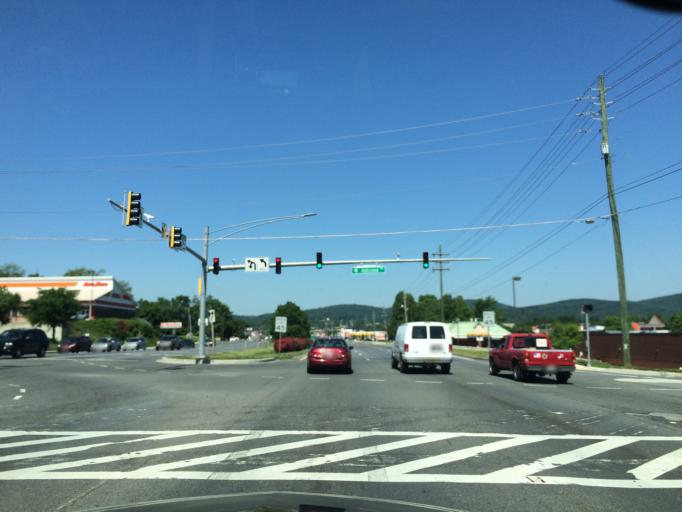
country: US
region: Maryland
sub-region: Frederick County
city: Frederick
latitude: 39.4177
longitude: -77.4455
